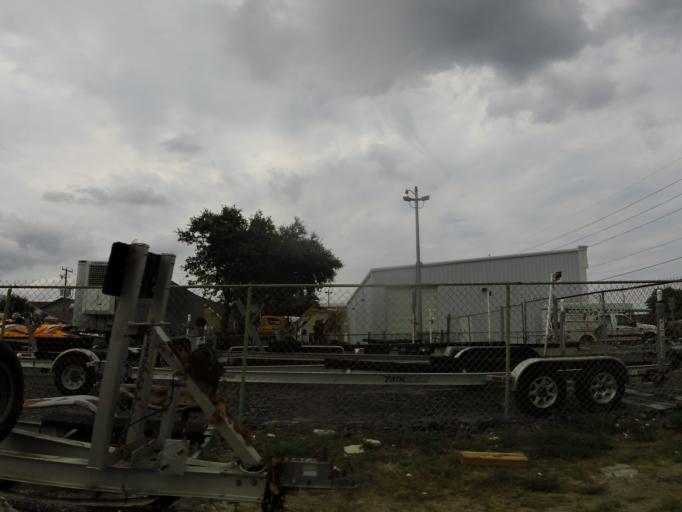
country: US
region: Florida
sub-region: Duval County
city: Atlantic Beach
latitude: 30.3299
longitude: -81.4176
